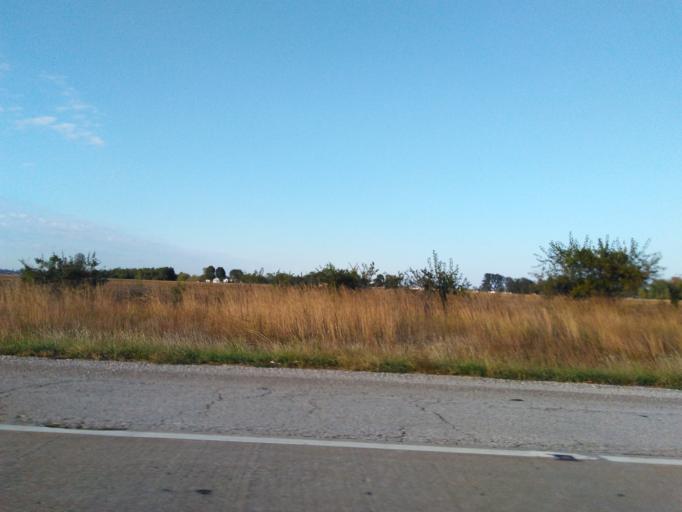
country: US
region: Illinois
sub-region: Saint Clair County
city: Dupo
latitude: 38.4769
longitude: -90.2419
